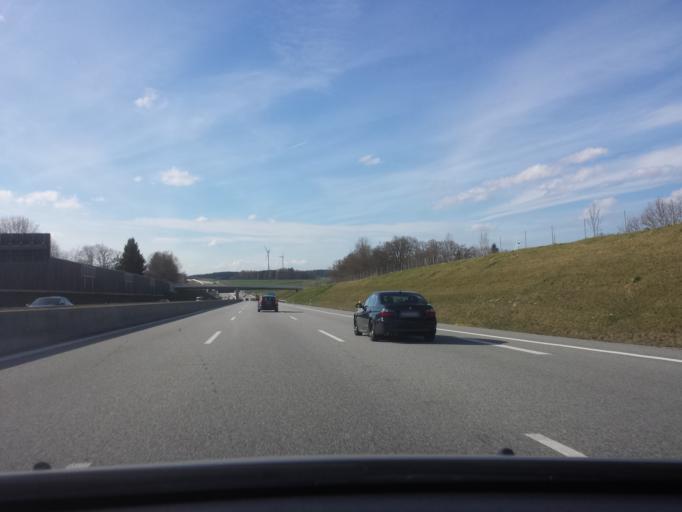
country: DE
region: Bavaria
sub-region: Upper Bavaria
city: Odelzhausen
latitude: 48.3106
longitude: 11.2035
